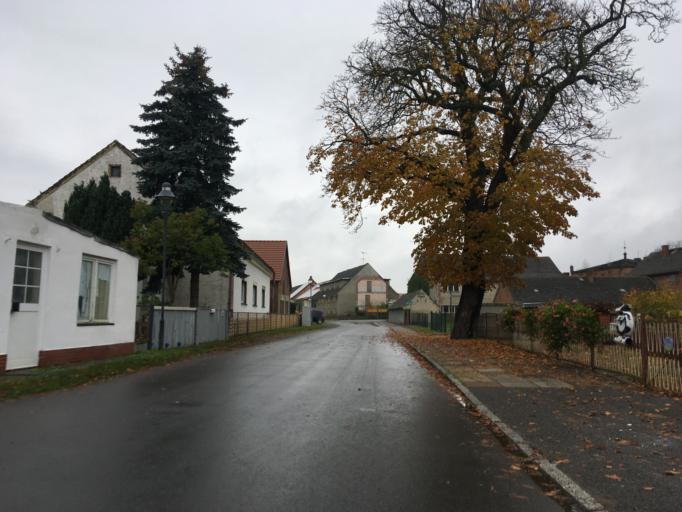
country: DE
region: Brandenburg
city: Tauche
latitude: 52.0836
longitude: 14.1713
